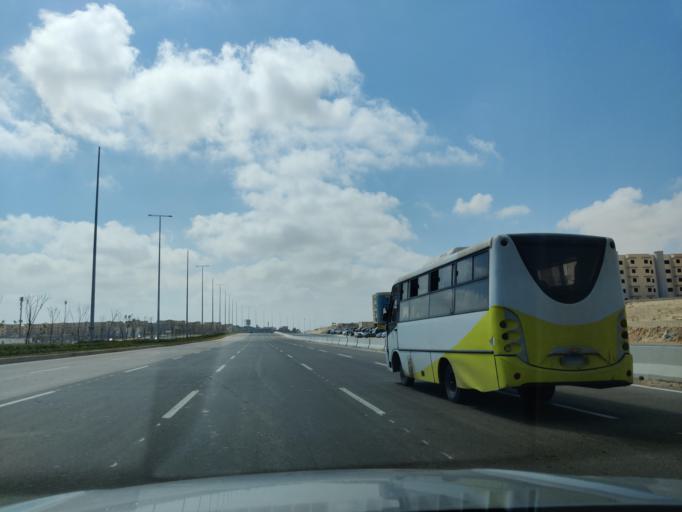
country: EG
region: Muhafazat Matruh
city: Al `Alamayn
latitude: 30.9580
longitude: 28.7621
